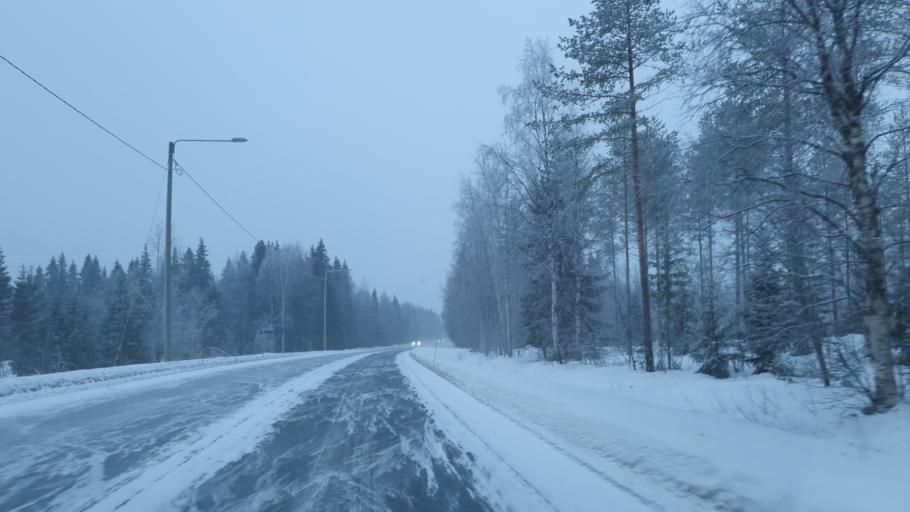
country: FI
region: Lapland
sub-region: Kemi-Tornio
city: Tornio
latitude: 65.9700
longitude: 24.0622
